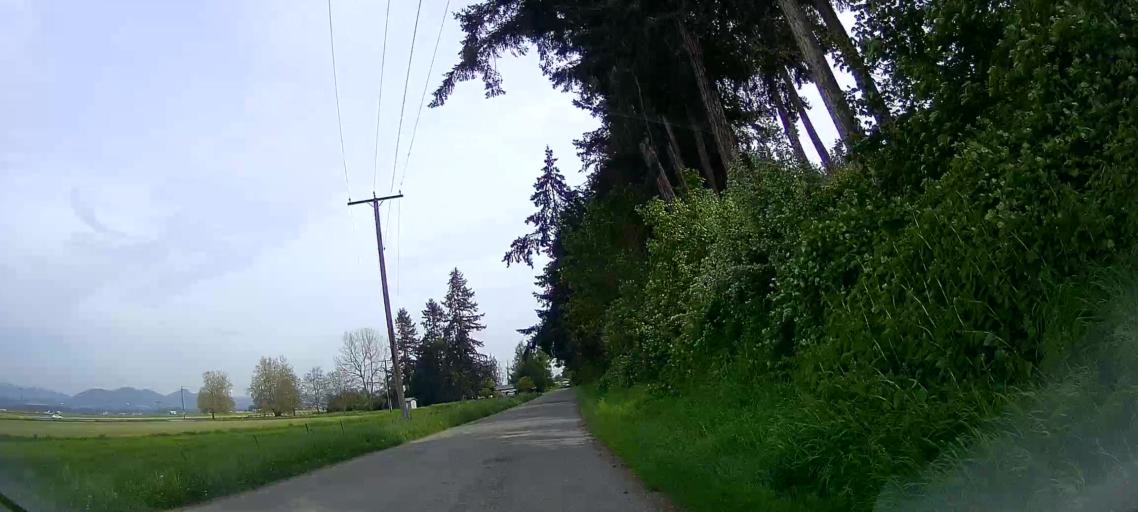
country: US
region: Washington
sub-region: Skagit County
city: Mount Vernon
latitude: 48.3948
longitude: -122.4465
